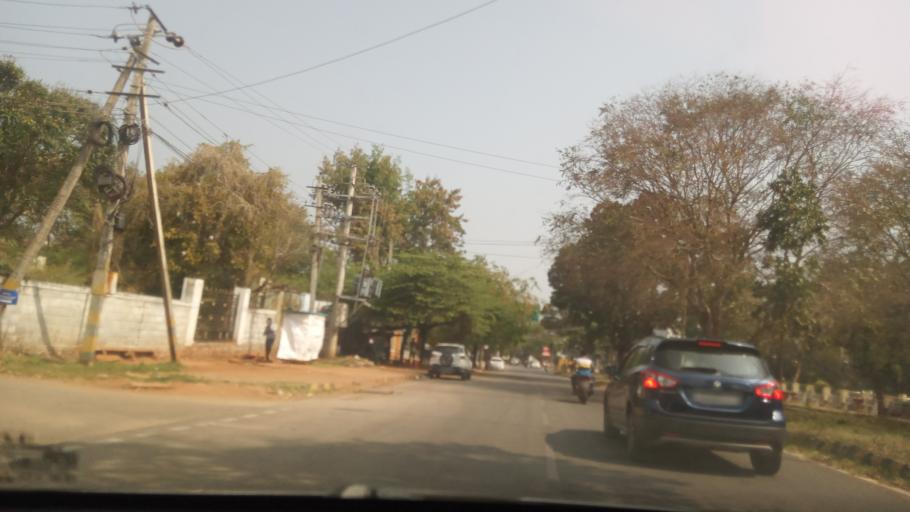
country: IN
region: Karnataka
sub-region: Mysore
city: Mysore
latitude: 12.2926
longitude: 76.6245
